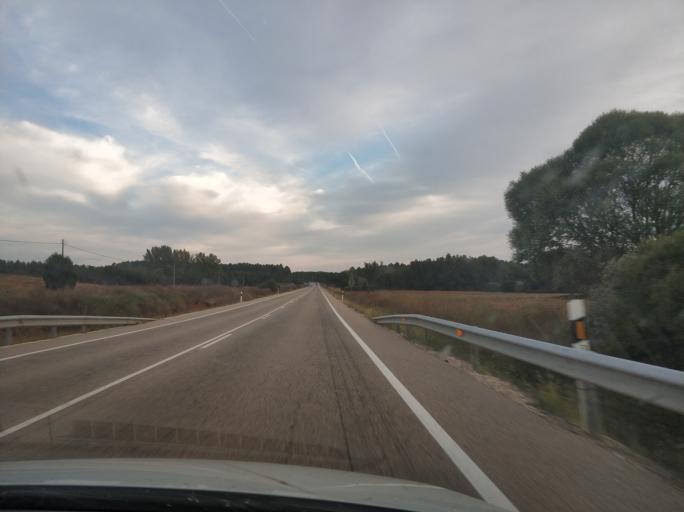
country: ES
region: Castille and Leon
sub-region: Provincia de Burgos
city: Hacinas
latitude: 41.9525
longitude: -3.2915
